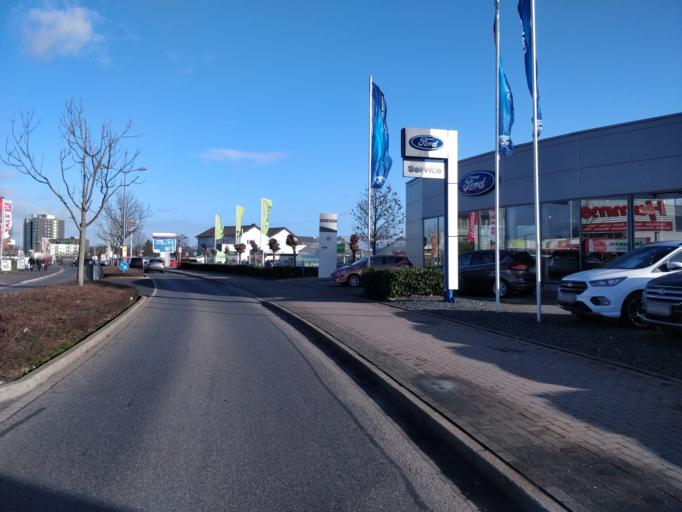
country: DE
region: North Rhine-Westphalia
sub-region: Regierungsbezirk Dusseldorf
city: Dormagen
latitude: 51.0916
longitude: 6.8133
